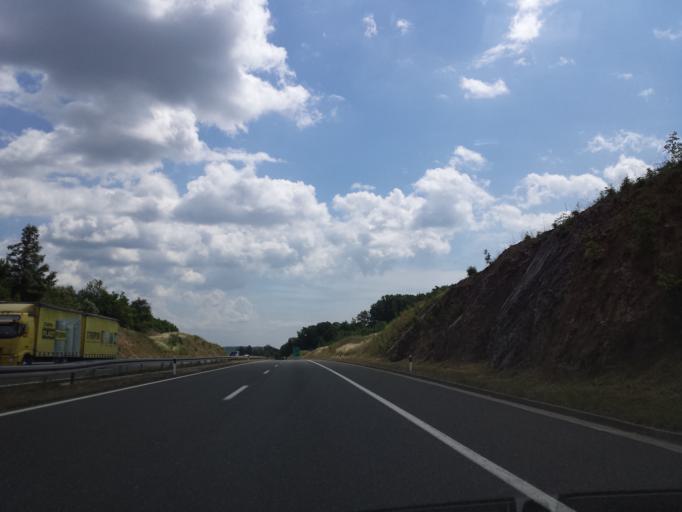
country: HR
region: Karlovacka
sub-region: Grad Ogulin
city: Ogulin
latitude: 45.4004
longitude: 15.2263
